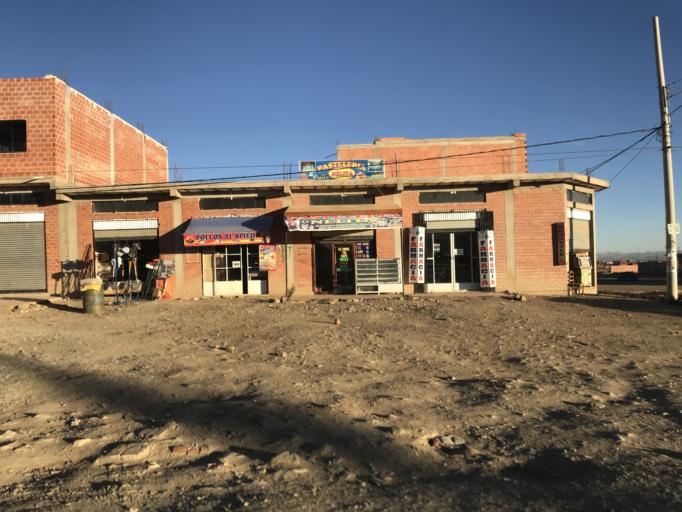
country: BO
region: La Paz
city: La Paz
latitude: -16.5064
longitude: -68.2566
